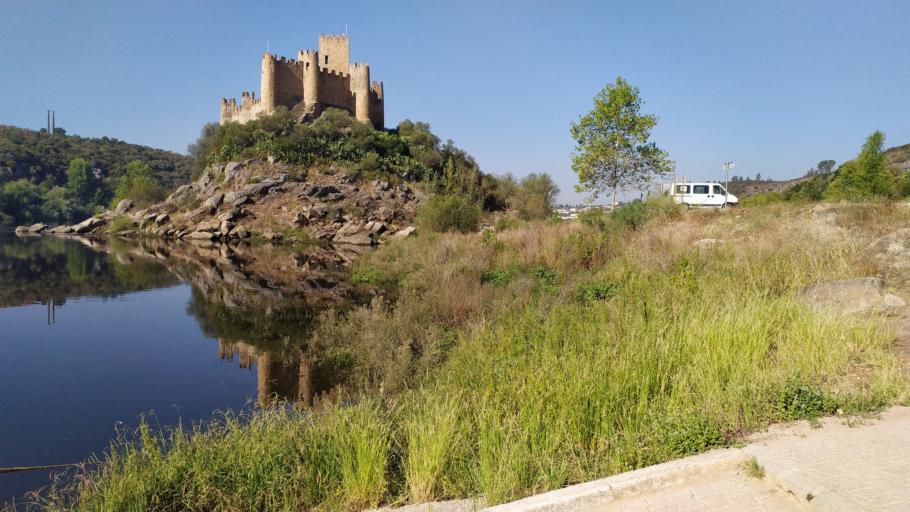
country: PT
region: Santarem
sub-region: Constancia
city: Constancia
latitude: 39.4628
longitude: -8.3823
